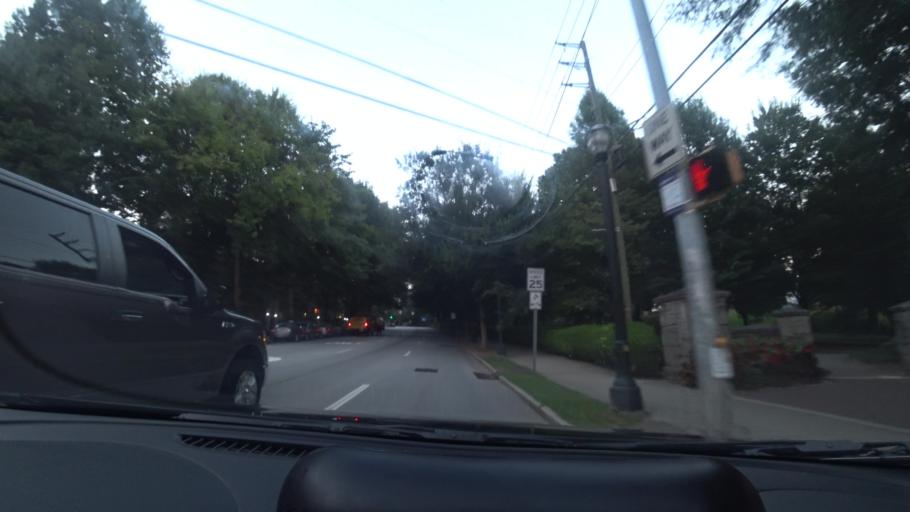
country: US
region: Georgia
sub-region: Fulton County
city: Atlanta
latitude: 33.7843
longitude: -84.3788
